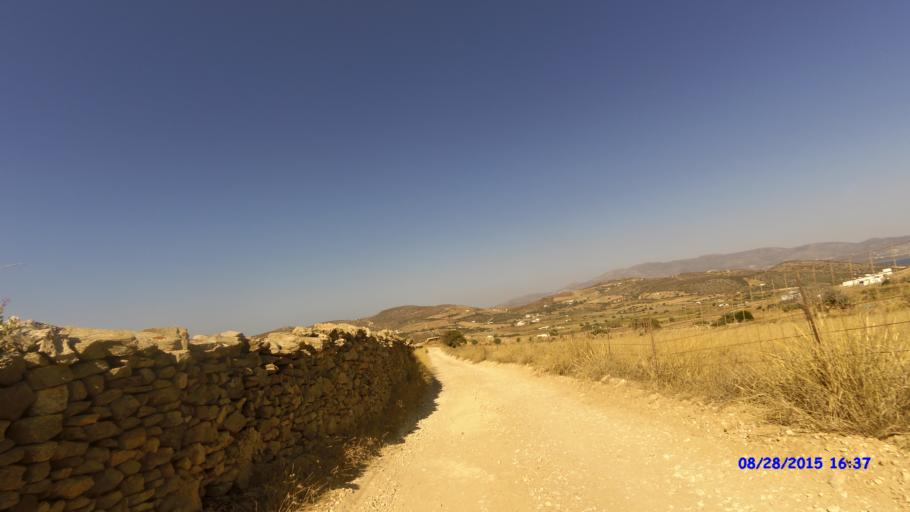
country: GR
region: South Aegean
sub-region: Nomos Kykladon
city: Antiparos
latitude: 37.0110
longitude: 25.0466
